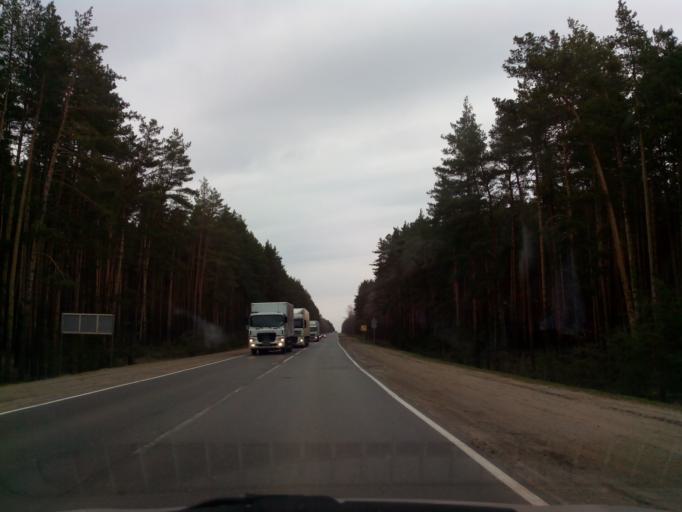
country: RU
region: Tambov
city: Znamenka
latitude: 52.5372
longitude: 41.3553
